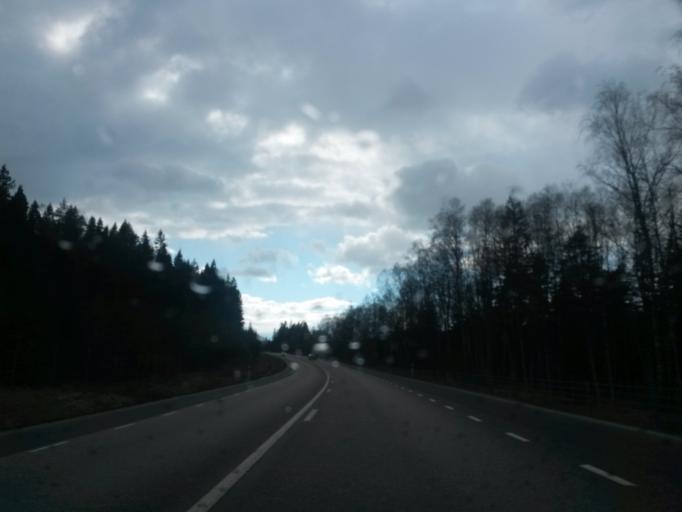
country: SE
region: Vaestra Goetaland
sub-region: Skovde Kommun
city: Skultorp
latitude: 58.3922
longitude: 13.7595
